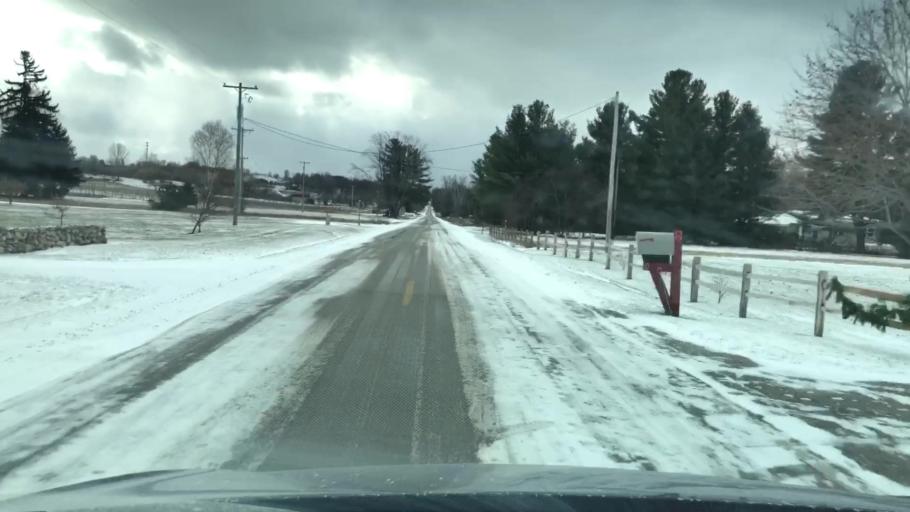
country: US
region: Michigan
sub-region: Antrim County
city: Elk Rapids
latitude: 44.9104
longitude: -85.5154
